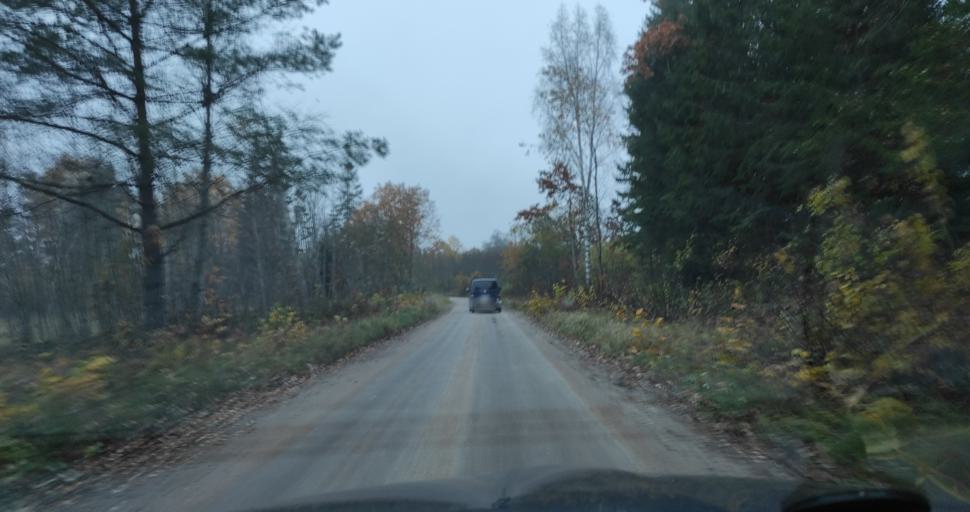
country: LV
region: Pavilostas
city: Pavilosta
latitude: 56.7611
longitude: 21.2736
